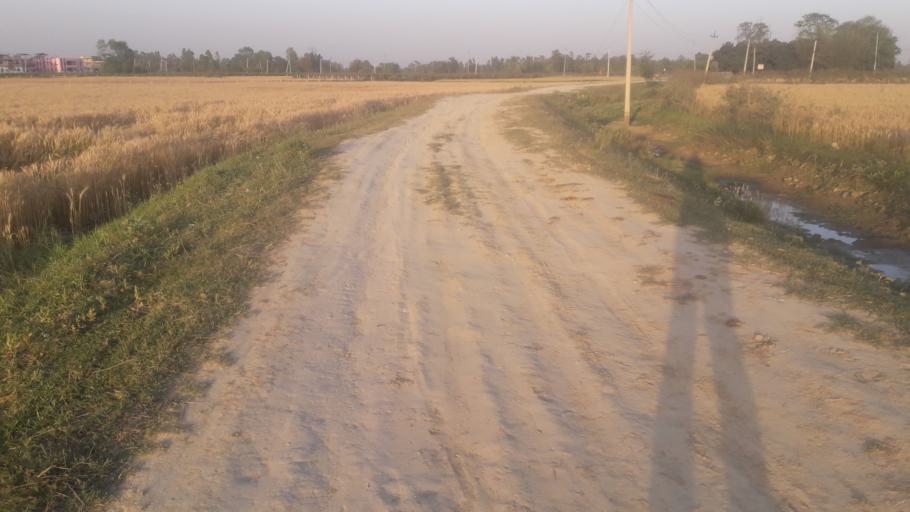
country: NP
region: Eastern Region
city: Siraha
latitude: 26.6315
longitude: 86.1947
